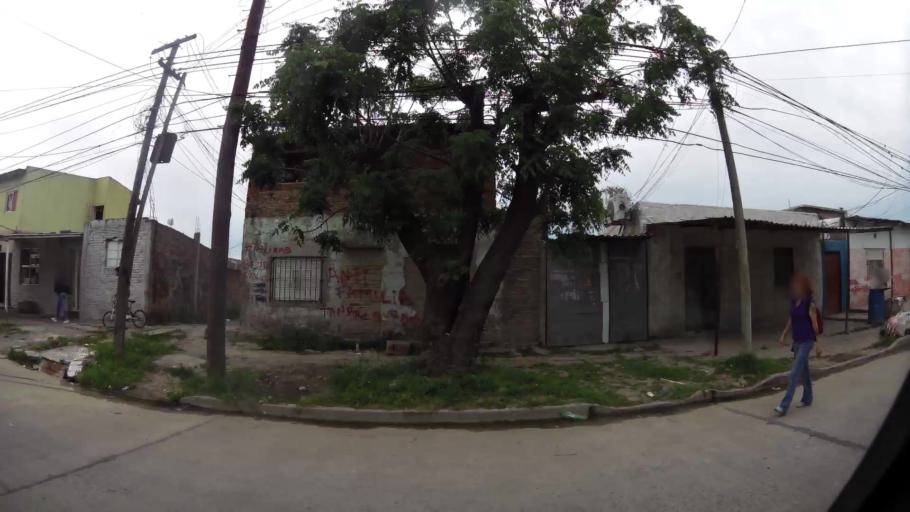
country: AR
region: Buenos Aires
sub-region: Partido de Avellaneda
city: Avellaneda
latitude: -34.6515
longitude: -58.3594
